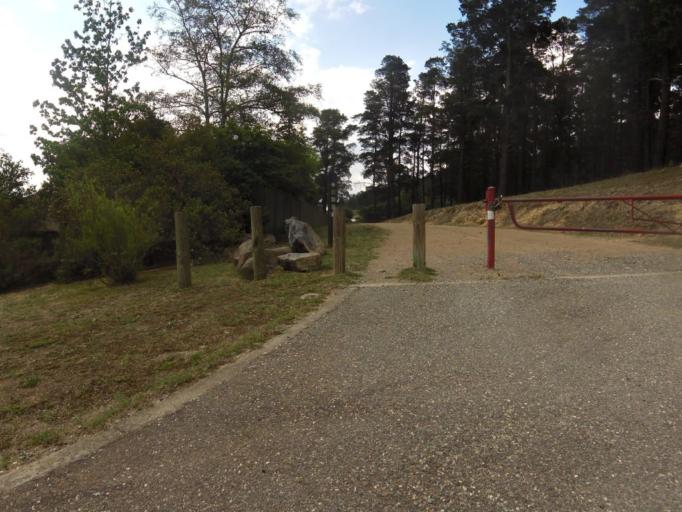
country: AU
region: Australian Capital Territory
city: Macarthur
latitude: -35.3711
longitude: 149.1164
